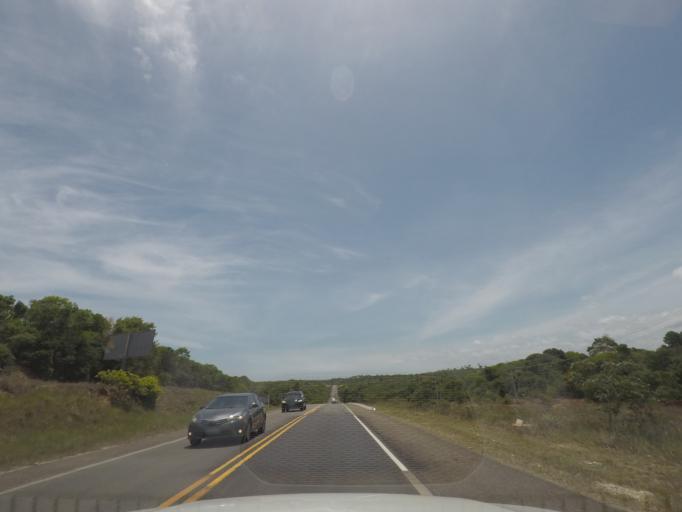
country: BR
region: Bahia
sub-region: Mata De Sao Joao
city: Mata de Sao Joao
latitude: -12.4192
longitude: -37.9324
